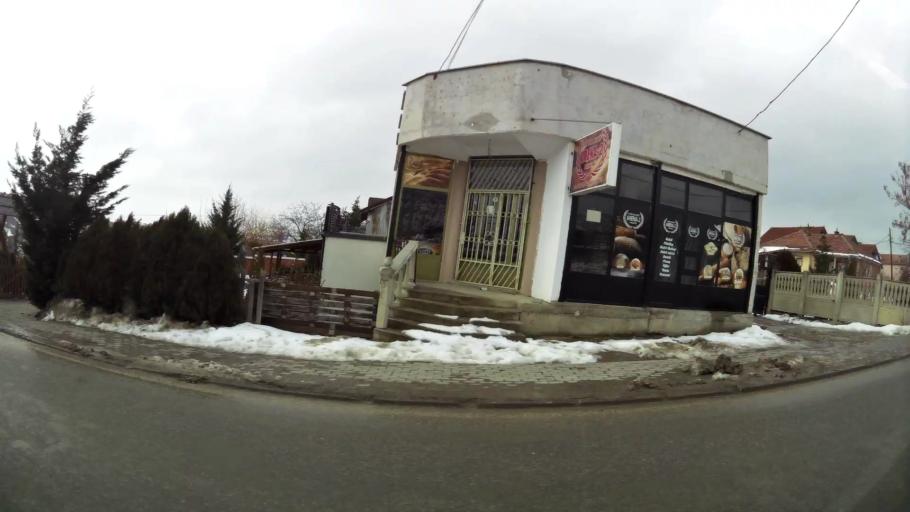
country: XK
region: Pristina
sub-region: Komuna e Prishtines
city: Pristina
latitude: 42.6462
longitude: 21.1953
